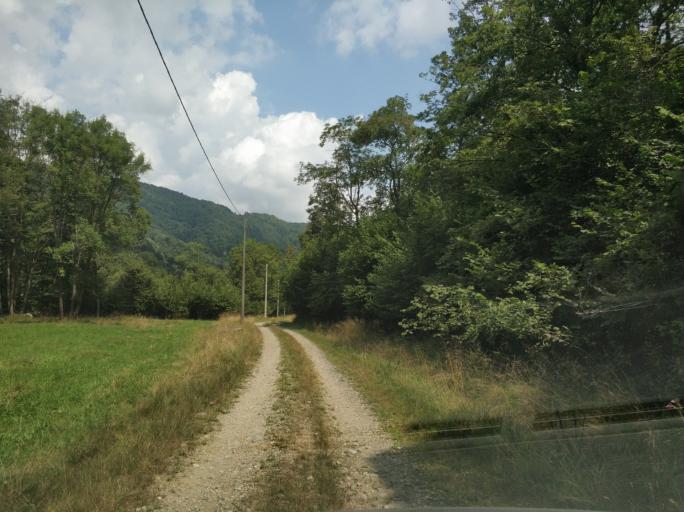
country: IT
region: Piedmont
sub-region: Provincia di Torino
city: Viu
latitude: 45.2081
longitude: 7.3940
